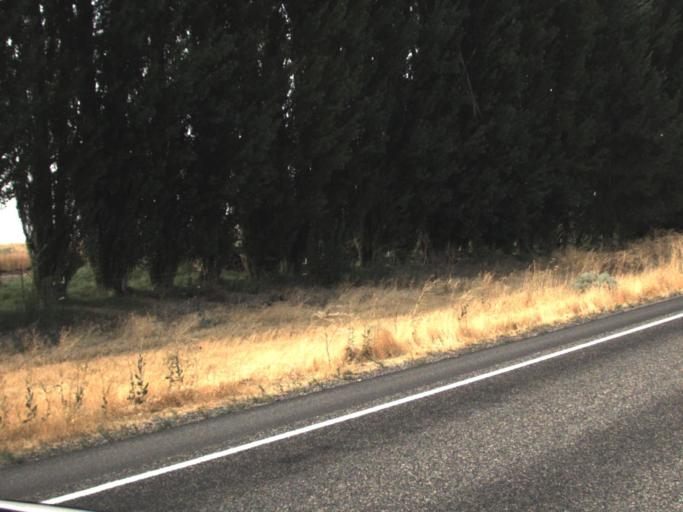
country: US
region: Oregon
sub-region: Morrow County
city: Irrigon
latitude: 45.9983
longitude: -119.6029
